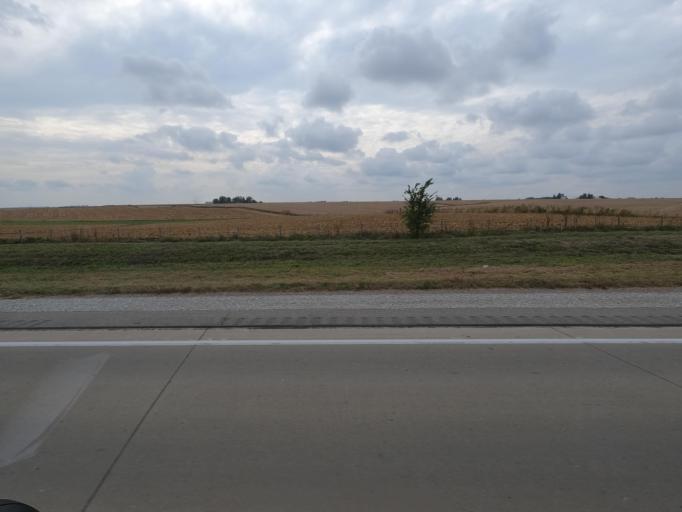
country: US
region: Iowa
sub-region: Jasper County
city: Monroe
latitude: 41.5589
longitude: -93.1484
